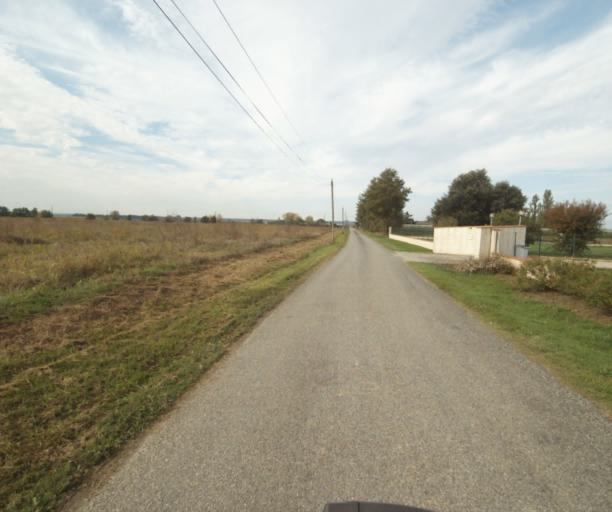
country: FR
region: Midi-Pyrenees
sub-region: Departement du Tarn-et-Garonne
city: Montech
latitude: 43.9419
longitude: 1.2327
